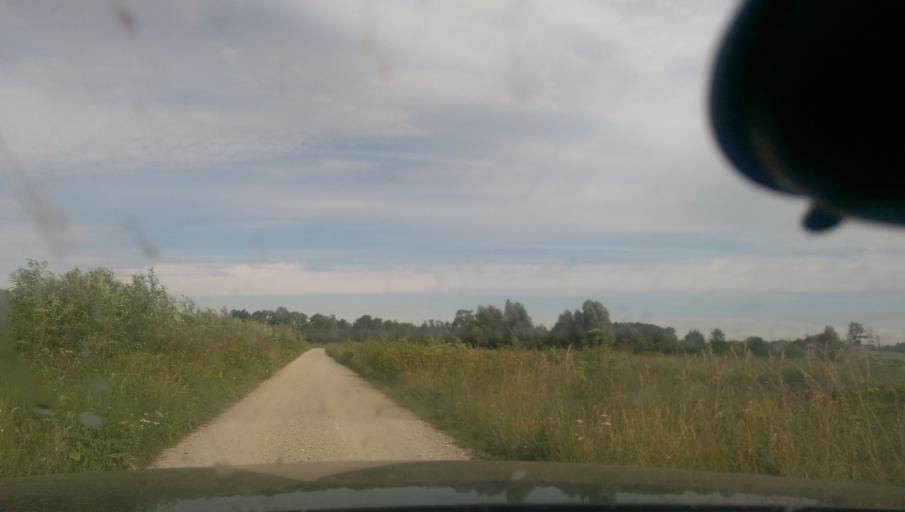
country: LT
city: Rusne
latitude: 55.2945
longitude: 21.3488
